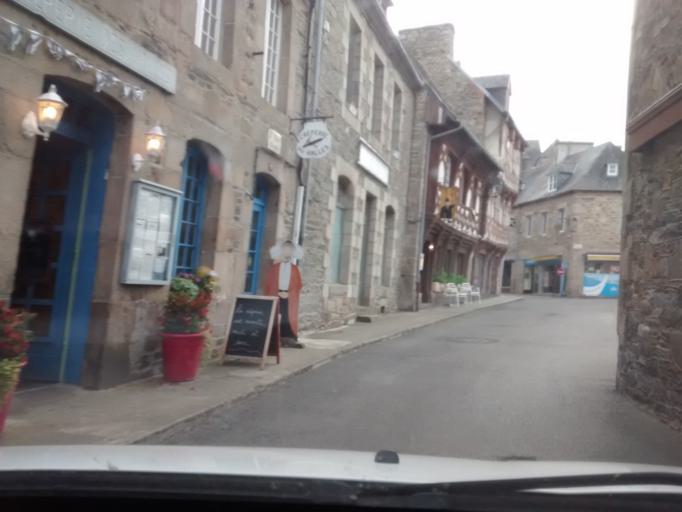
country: FR
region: Brittany
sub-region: Departement des Cotes-d'Armor
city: Treguier
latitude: 48.7880
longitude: -3.2293
